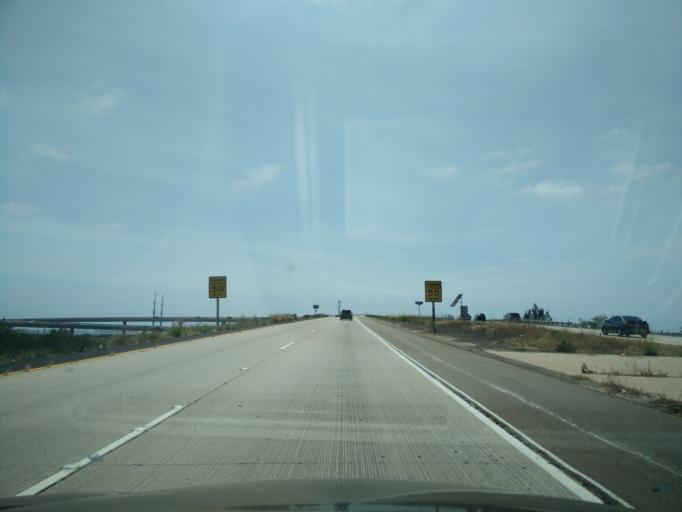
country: US
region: California
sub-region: San Diego County
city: Chula Vista
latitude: 32.6529
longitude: -117.0999
